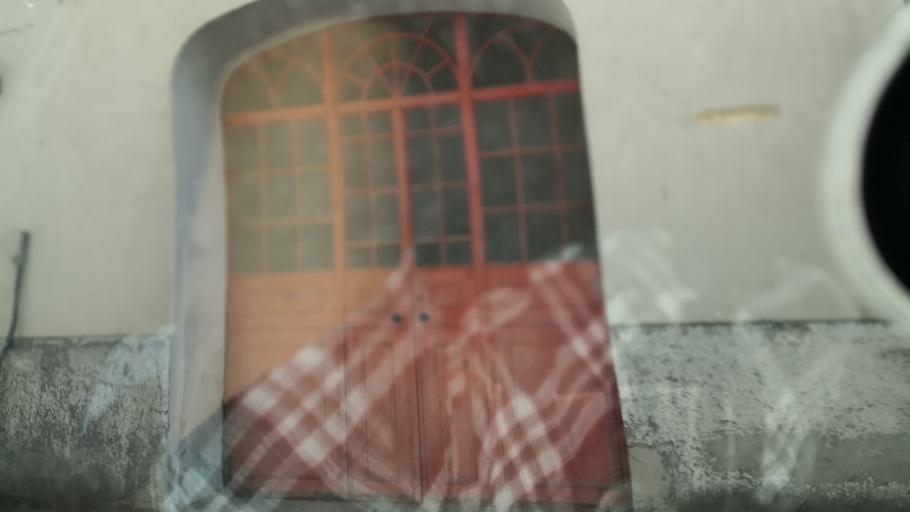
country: PT
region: Braganca
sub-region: Braganca Municipality
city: Braganca
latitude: 41.8023
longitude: -6.7596
